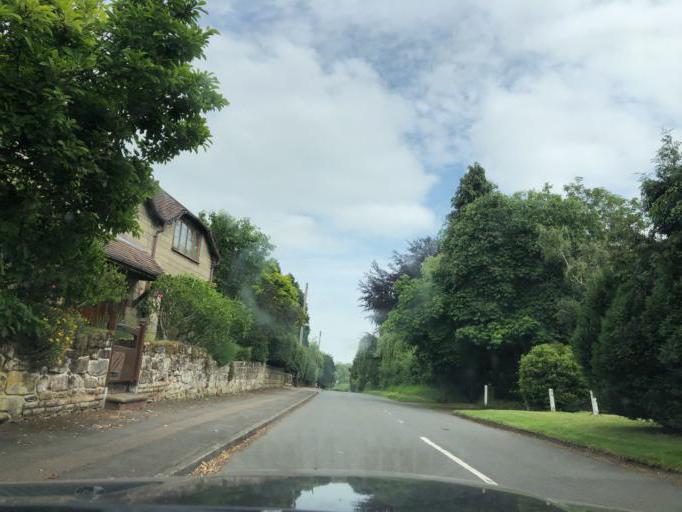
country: GB
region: England
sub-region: Warwickshire
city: Kenilworth
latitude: 52.3177
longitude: -1.5766
